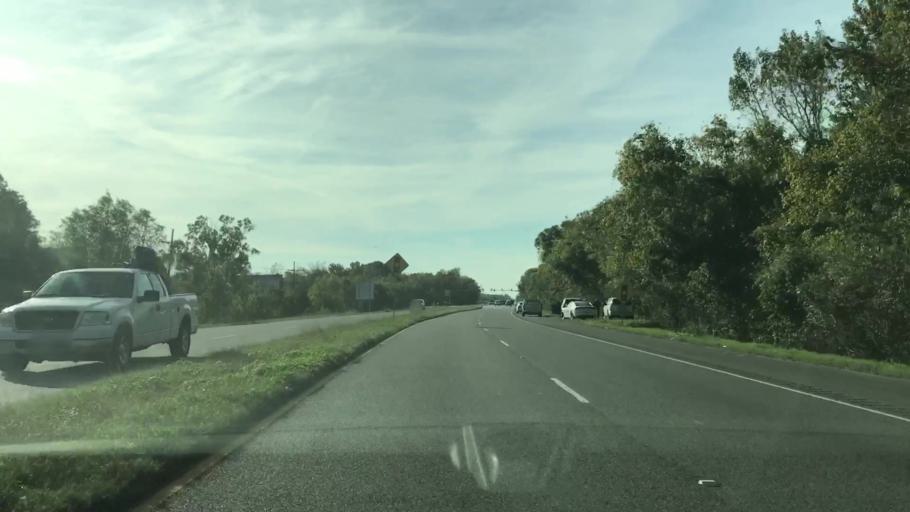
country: US
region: Louisiana
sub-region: Jefferson Parish
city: Avondale
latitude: 29.9092
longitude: -90.1883
